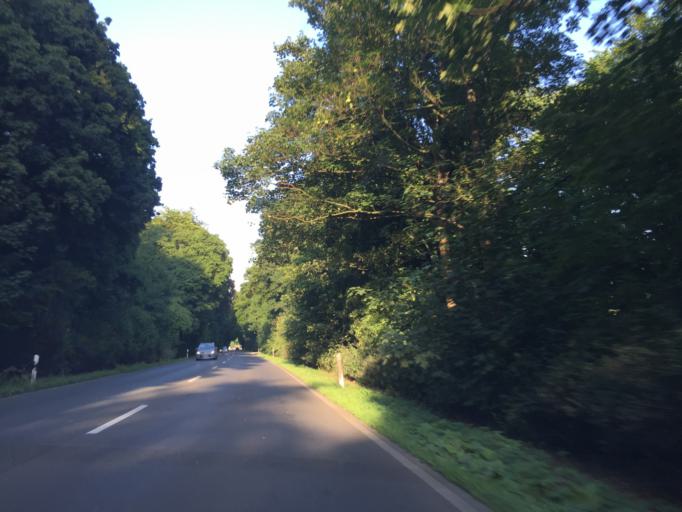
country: DE
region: North Rhine-Westphalia
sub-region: Regierungsbezirk Koln
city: Neustadt/Sued
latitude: 50.8952
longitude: 6.9324
